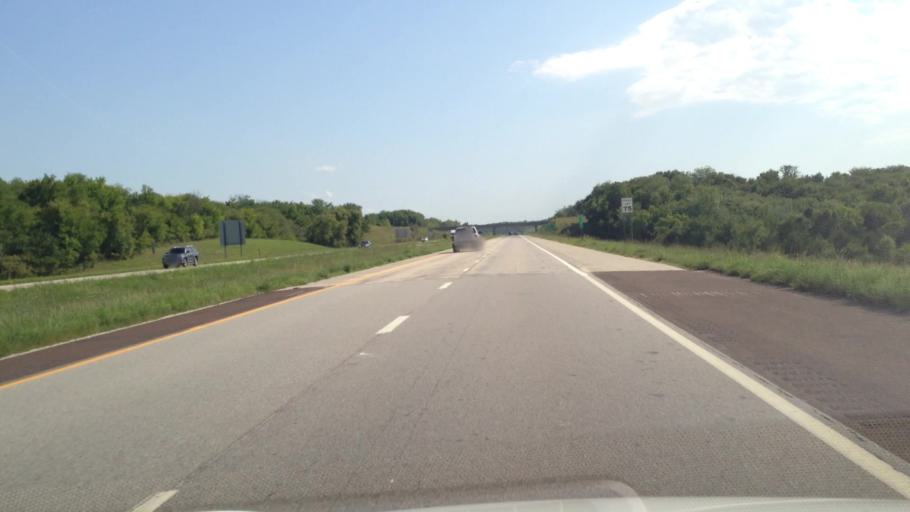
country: US
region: Kansas
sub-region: Miami County
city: Louisburg
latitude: 38.6125
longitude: -94.6947
